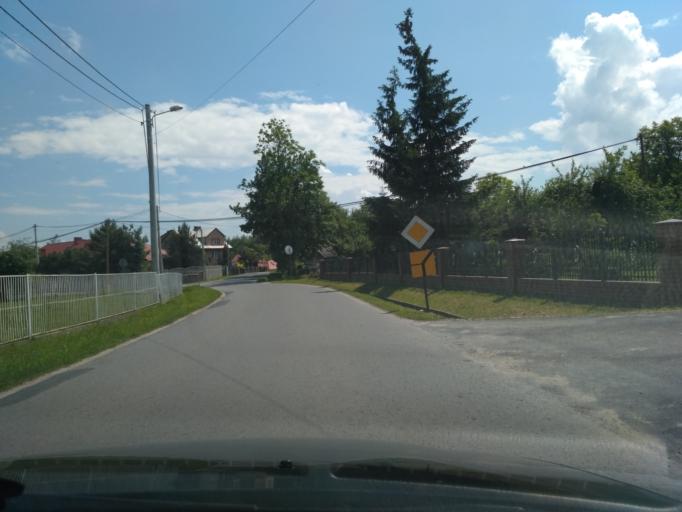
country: PL
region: Subcarpathian Voivodeship
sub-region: Powiat lancucki
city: Sonina
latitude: 50.0613
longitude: 22.2651
